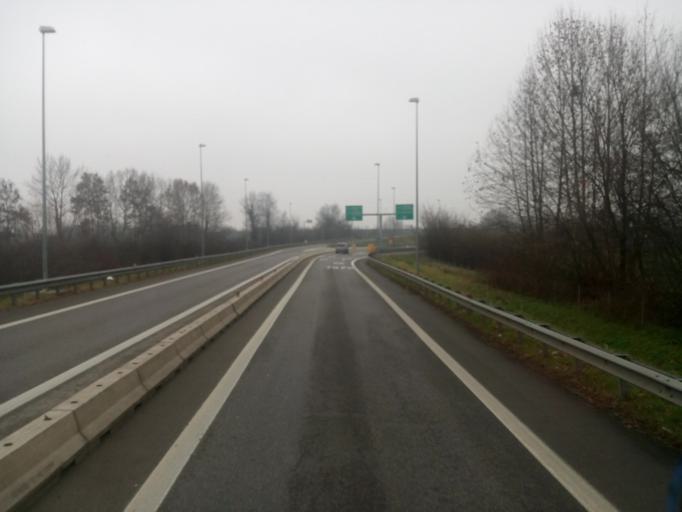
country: IT
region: Lombardy
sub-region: Provincia di Brescia
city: San Zeno Naviglio
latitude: 45.4699
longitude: 10.2174
